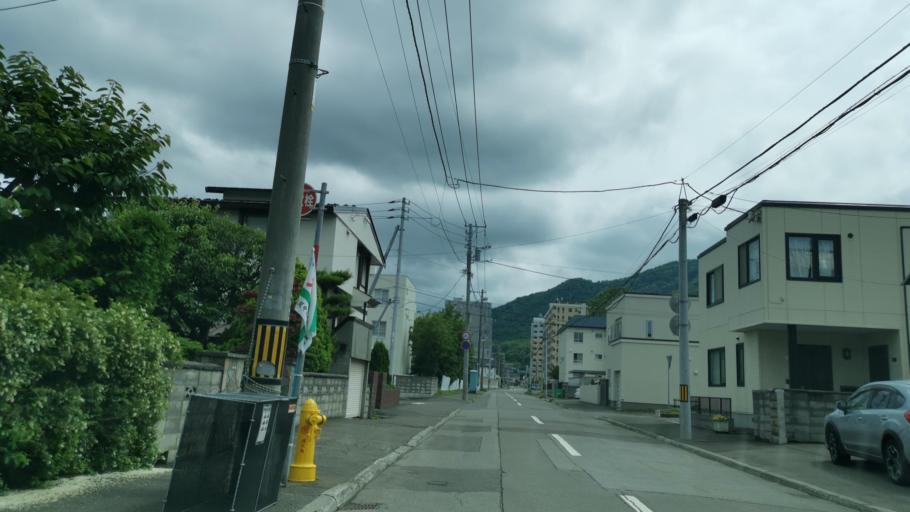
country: JP
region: Hokkaido
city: Sapporo
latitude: 43.0386
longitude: 141.3351
